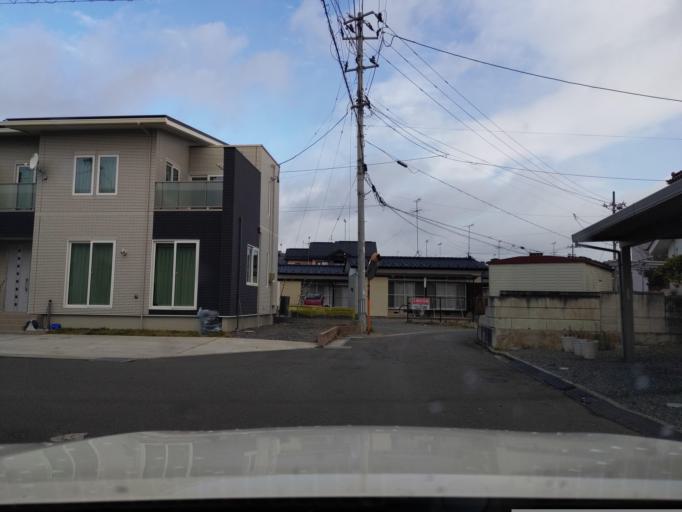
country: JP
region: Fukushima
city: Koriyama
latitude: 37.3752
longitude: 140.3608
